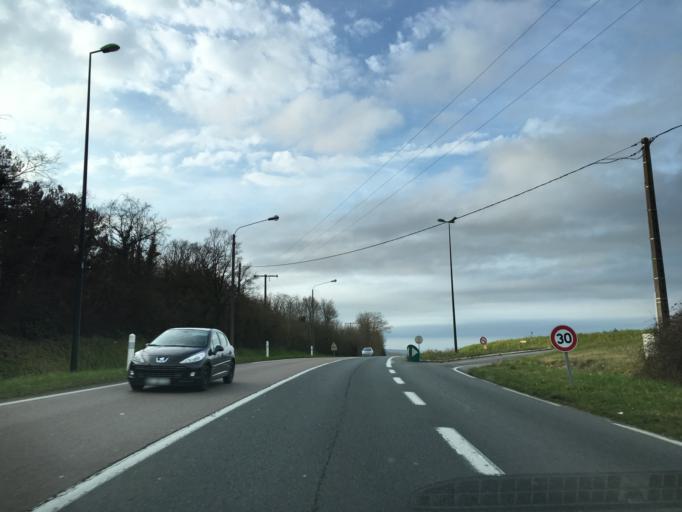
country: FR
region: Bourgogne
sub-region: Departement de l'Yonne
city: Maillot
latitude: 48.1563
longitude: 3.3059
